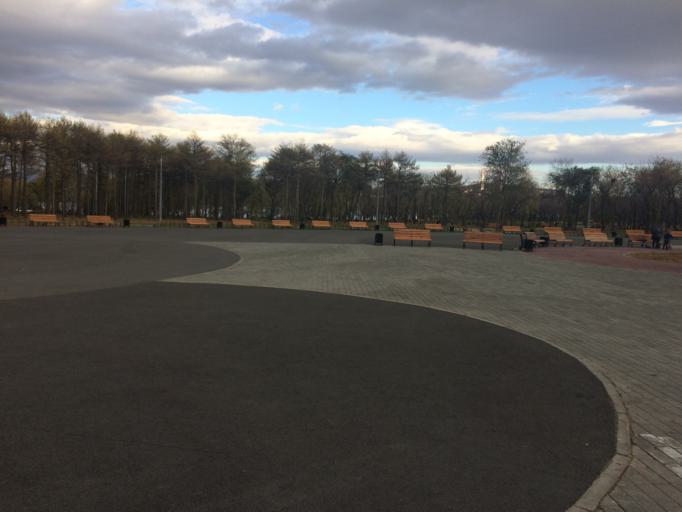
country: RU
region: Chelyabinsk
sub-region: Gorod Magnitogorsk
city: Magnitogorsk
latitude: 53.4045
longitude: 58.9888
